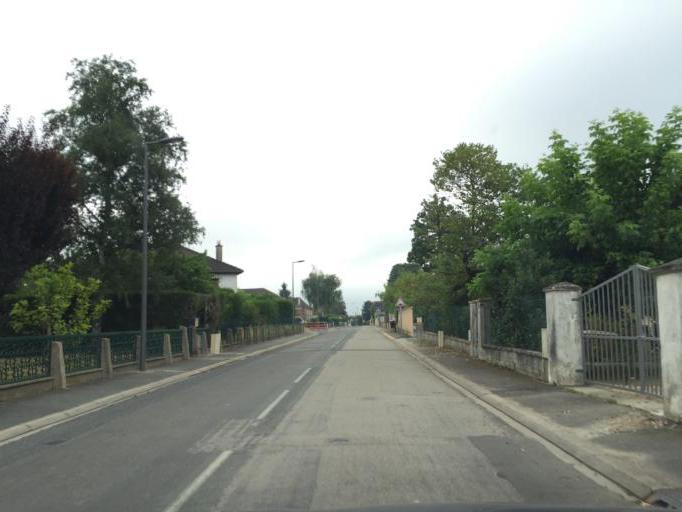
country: FR
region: Auvergne
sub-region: Departement de l'Allier
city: Avermes
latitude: 46.5857
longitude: 3.3131
